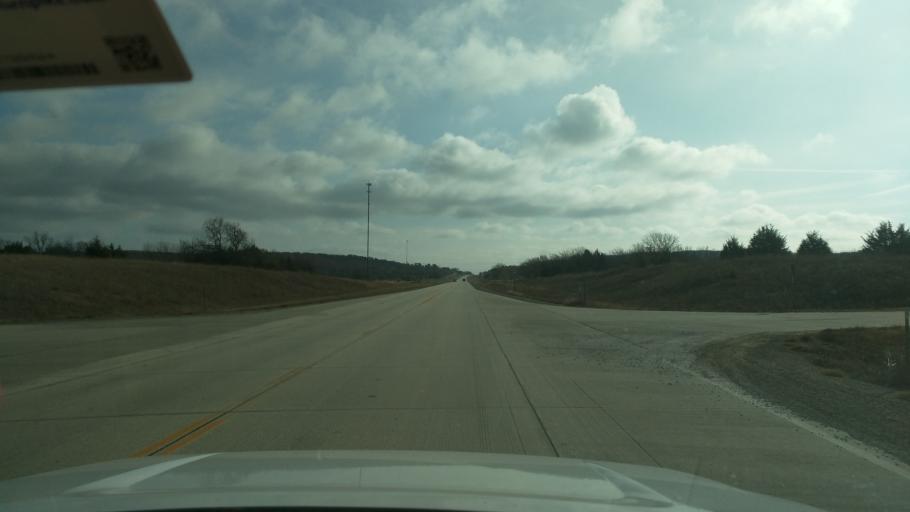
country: US
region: Kansas
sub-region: Chautauqua County
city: Sedan
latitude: 37.0796
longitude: -96.1008
